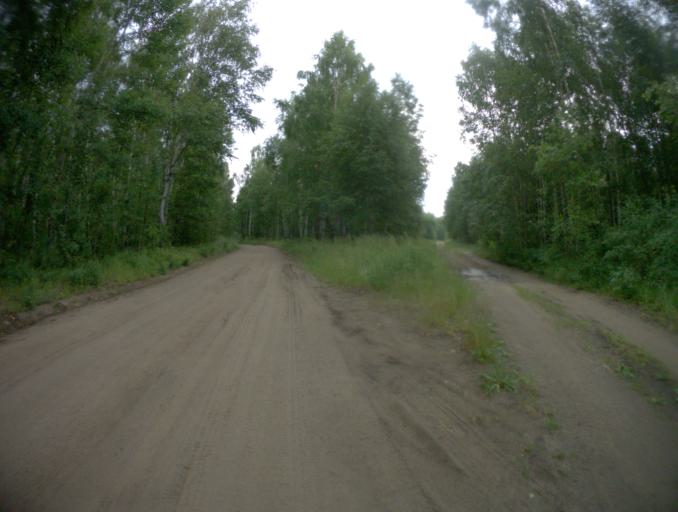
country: RU
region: Ivanovo
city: Talitsy
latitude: 56.6044
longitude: 42.4008
